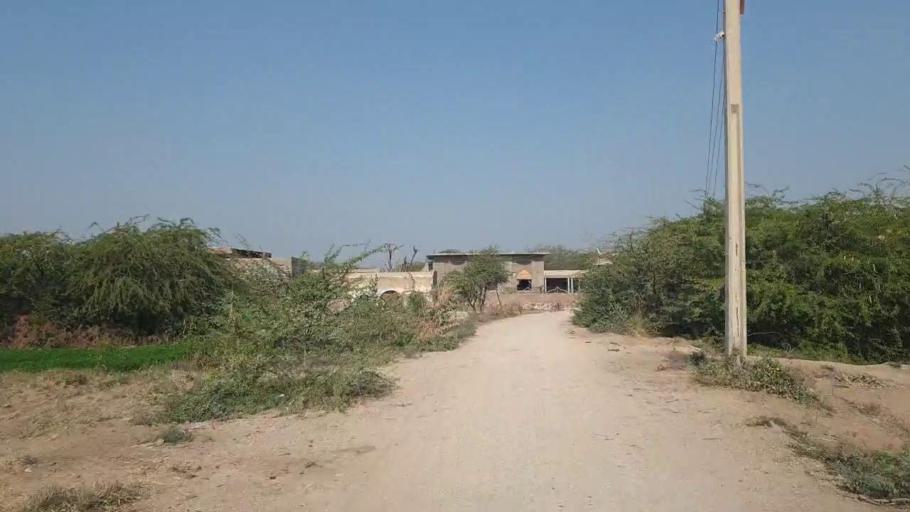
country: PK
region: Sindh
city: Chambar
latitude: 25.4092
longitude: 68.9083
